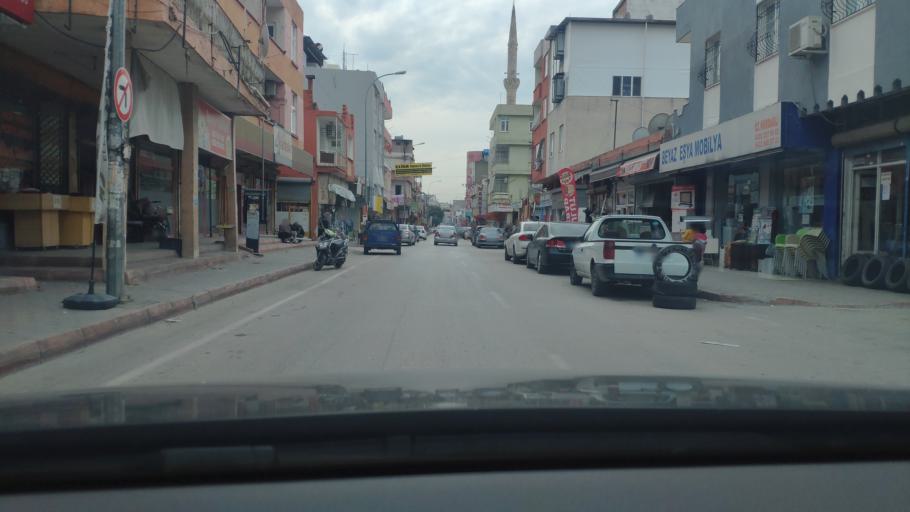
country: TR
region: Adana
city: Adana
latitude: 37.0160
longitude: 35.3144
